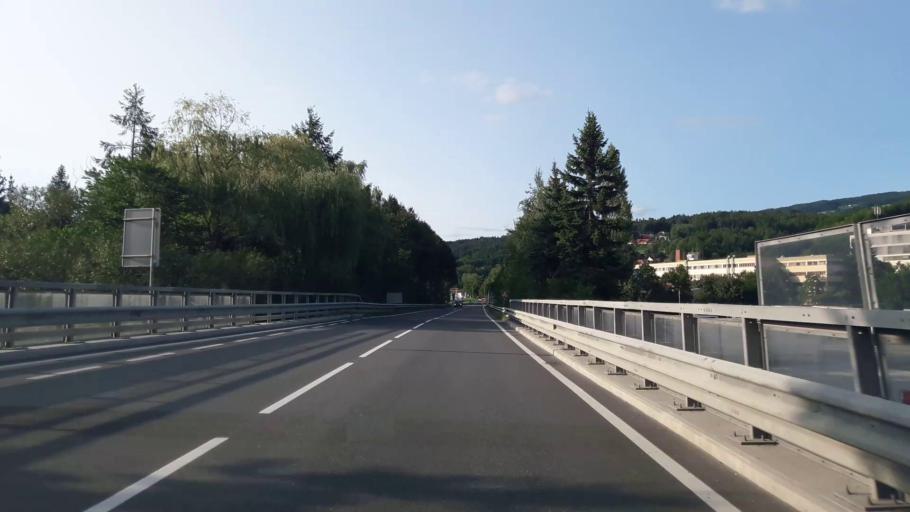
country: AT
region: Styria
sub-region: Politischer Bezirk Weiz
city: Anger
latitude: 47.2733
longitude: 15.6942
